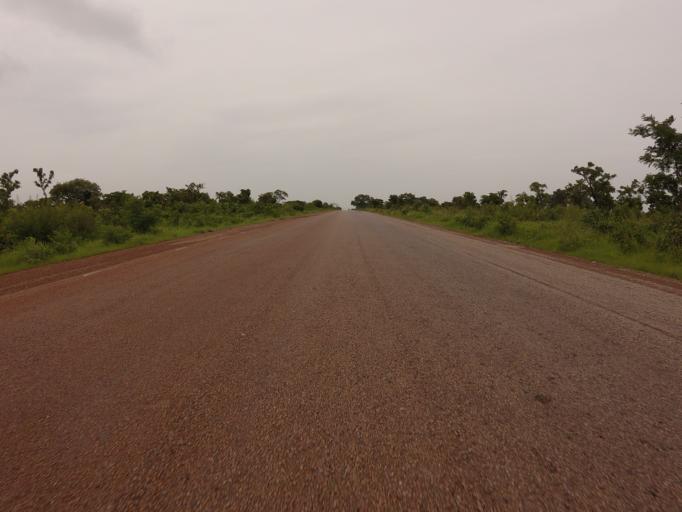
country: GH
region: Northern
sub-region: Yendi
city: Yendi
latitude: 9.3495
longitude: 0.0025
